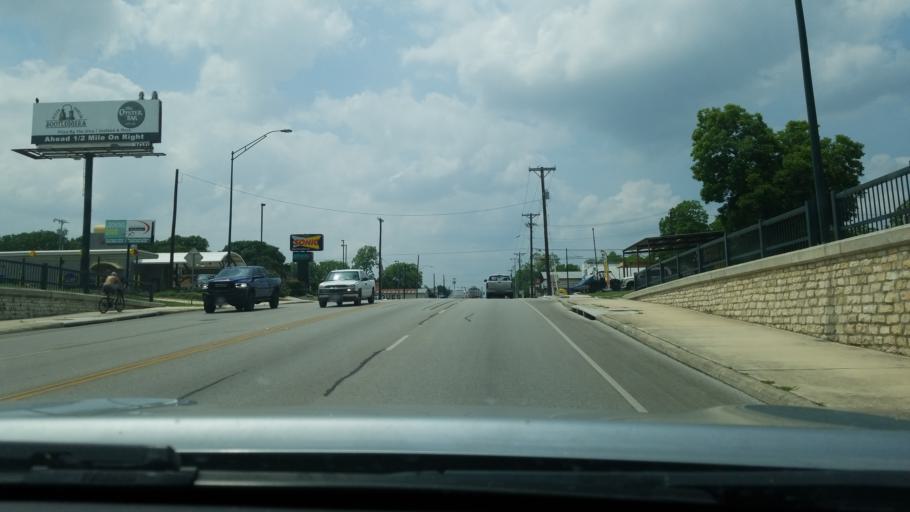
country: US
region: Texas
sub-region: Comal County
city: New Braunfels
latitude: 29.6964
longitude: -98.1149
